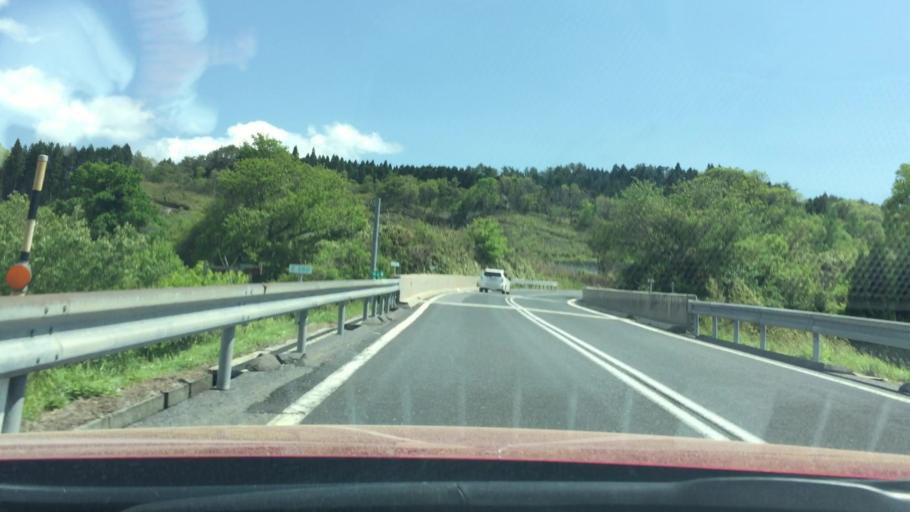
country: JP
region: Tottori
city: Kurayoshi
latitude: 35.2754
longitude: 133.6224
